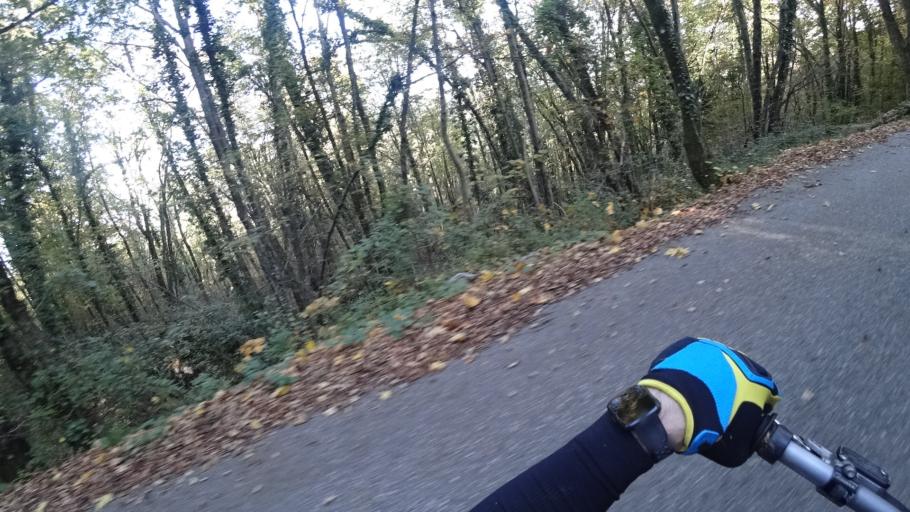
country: HR
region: Primorsko-Goranska
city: Matulji
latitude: 45.3874
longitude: 14.2882
